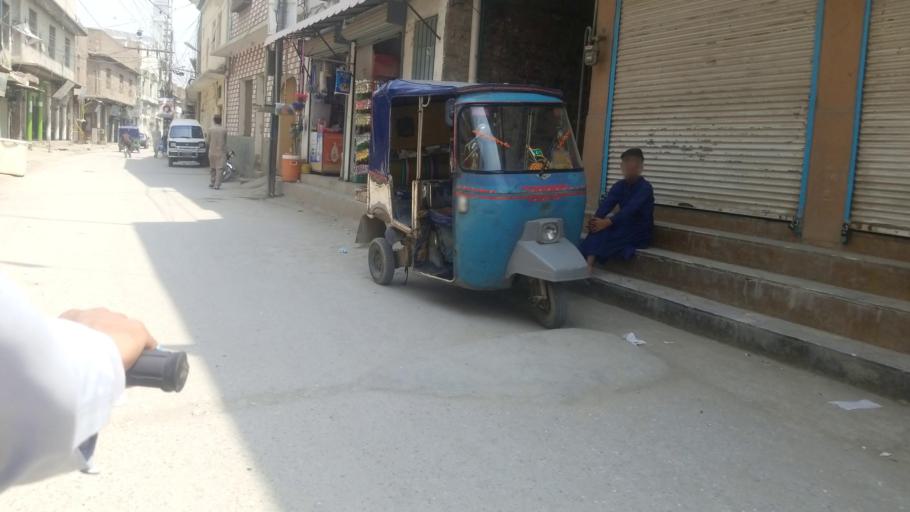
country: PK
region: Khyber Pakhtunkhwa
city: Peshawar
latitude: 34.0277
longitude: 71.5830
